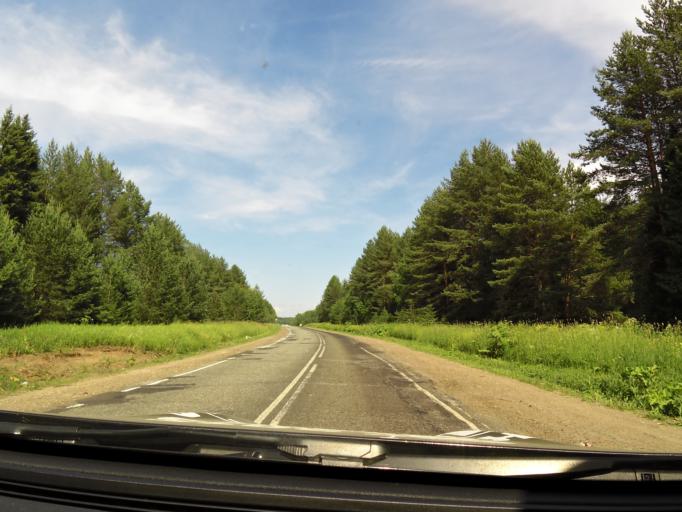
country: RU
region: Kirov
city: Slobodskoy
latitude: 58.7811
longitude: 50.4851
